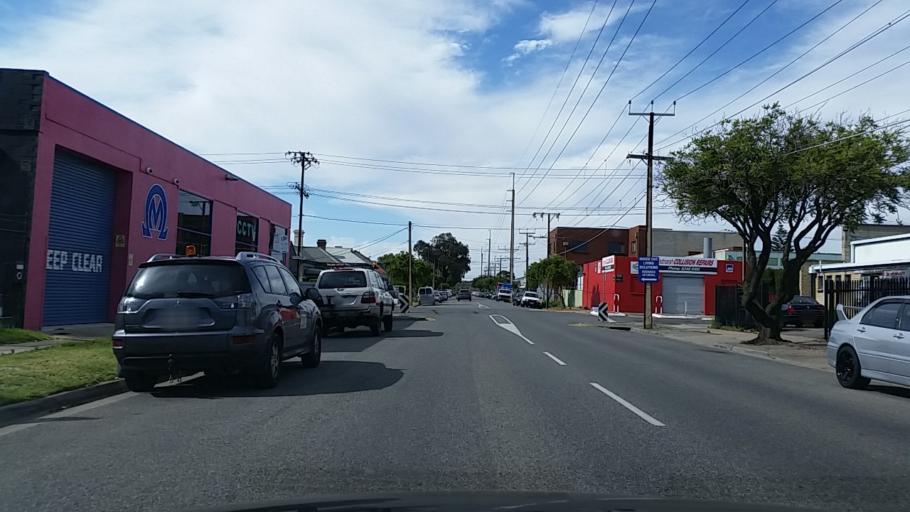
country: AU
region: South Australia
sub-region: City of West Torrens
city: Thebarton
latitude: -34.9084
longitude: 138.5665
